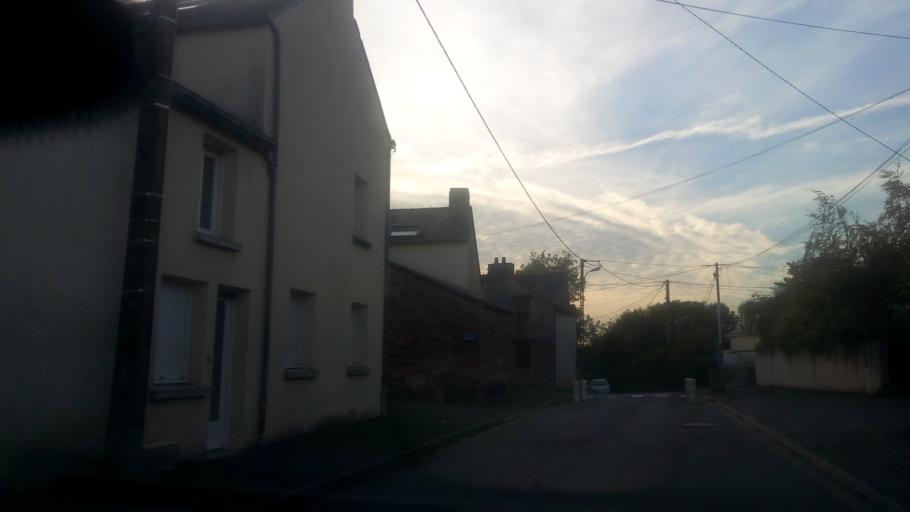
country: FR
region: Brittany
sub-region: Departement d'Ille-et-Vilaine
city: Redon
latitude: 47.6613
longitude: -2.0908
